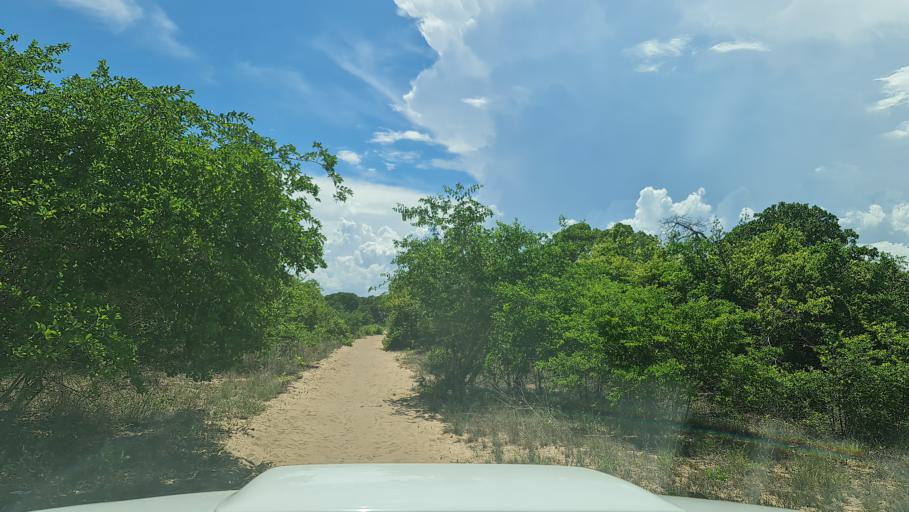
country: MZ
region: Nampula
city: Antonio Enes
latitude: -15.7065
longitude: 40.2592
